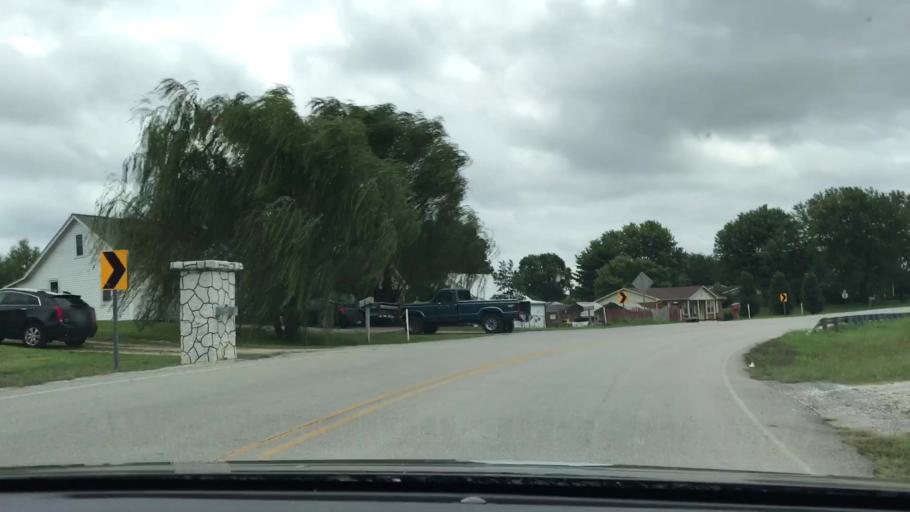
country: US
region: Kentucky
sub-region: Barren County
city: Glasgow
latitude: 36.9767
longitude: -85.8879
